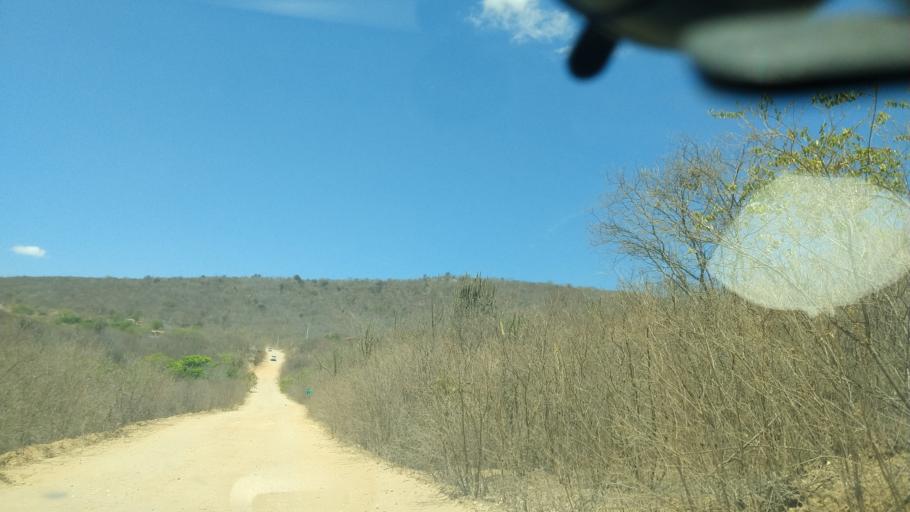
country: BR
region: Rio Grande do Norte
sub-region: Cerro Cora
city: Cerro Cora
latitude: -6.0136
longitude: -36.3154
